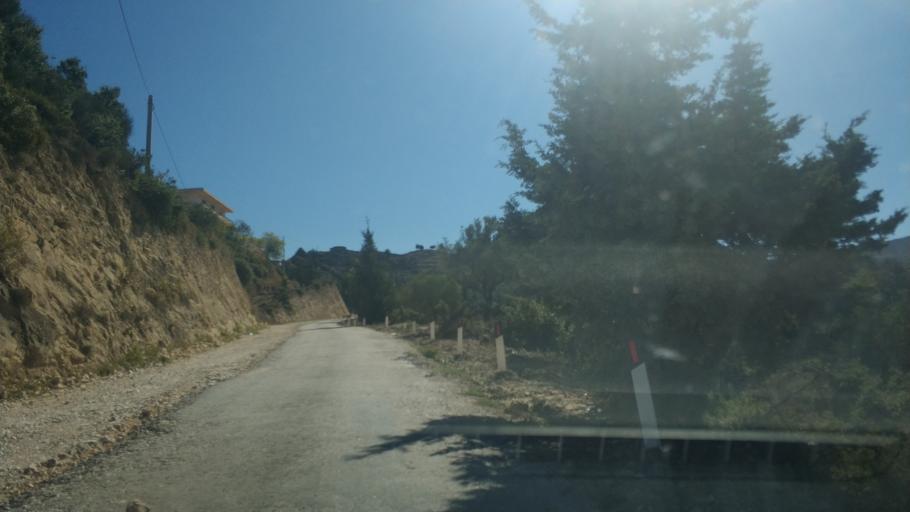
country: AL
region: Vlore
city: Vlore
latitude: 40.4483
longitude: 19.5163
